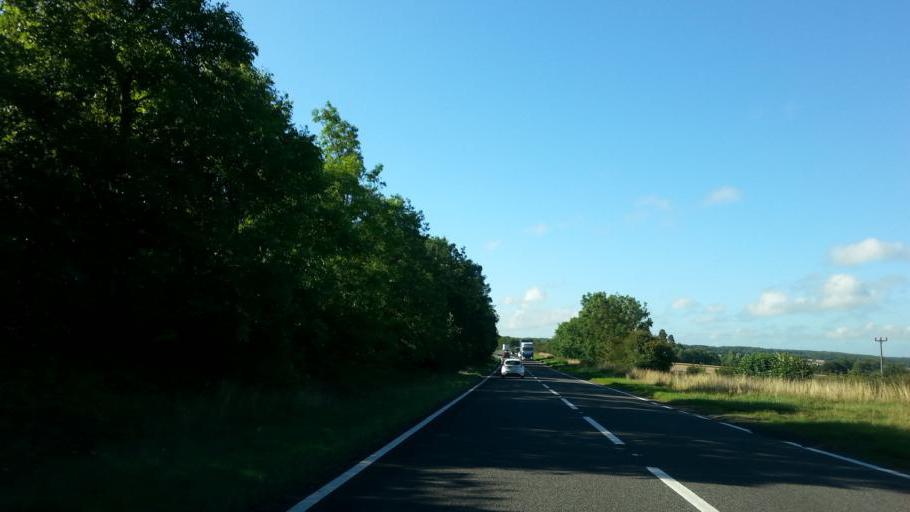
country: GB
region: England
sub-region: District of Rutland
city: Ketton
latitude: 52.6052
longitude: -0.5361
